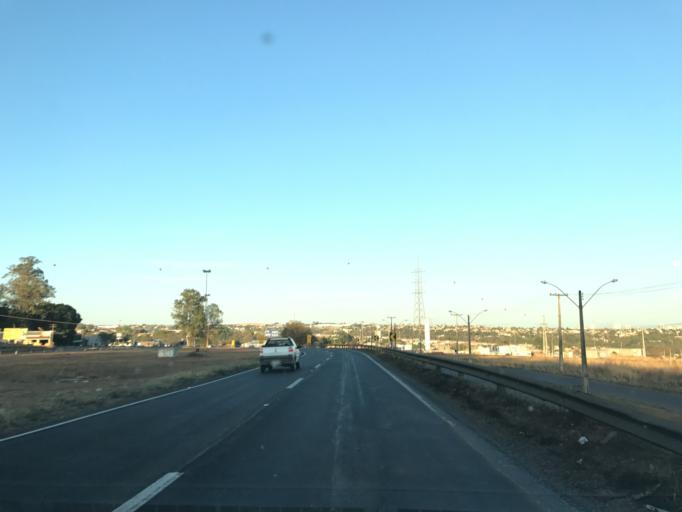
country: BR
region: Goias
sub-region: Anapolis
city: Anapolis
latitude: -16.3349
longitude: -48.8942
